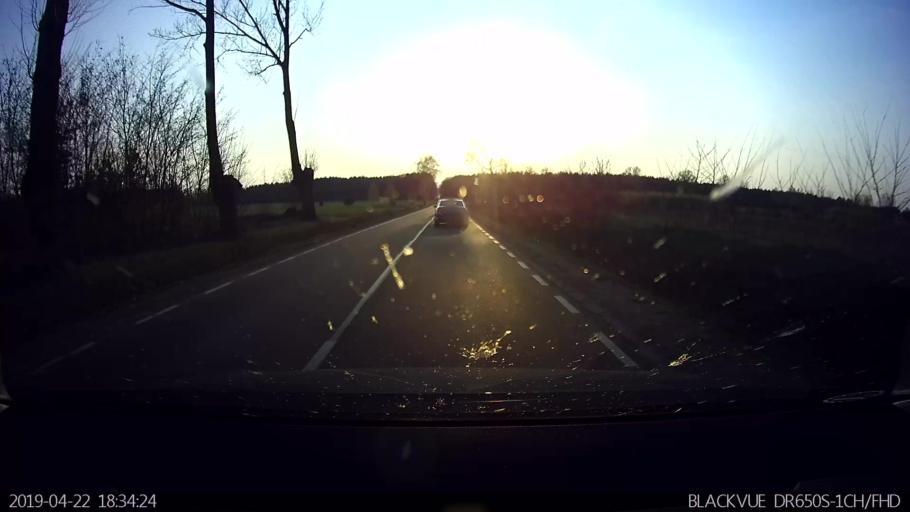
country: PL
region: Masovian Voivodeship
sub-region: Powiat wolominski
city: Jasienica
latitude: 52.4452
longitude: 21.3694
